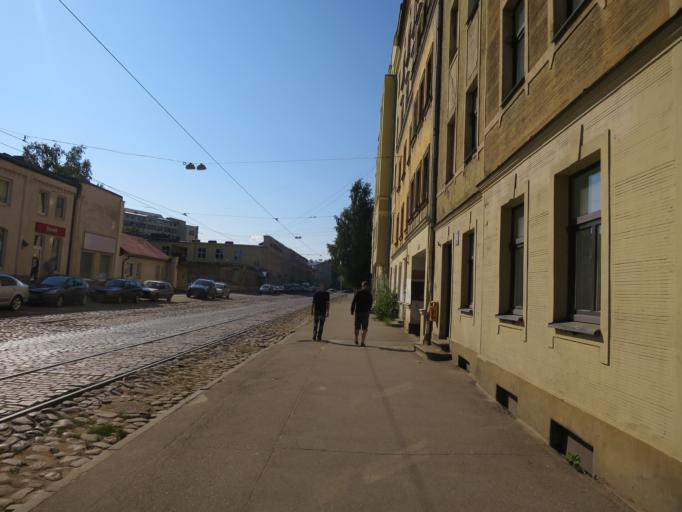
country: LV
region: Riga
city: Riga
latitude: 56.9674
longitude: 24.1505
